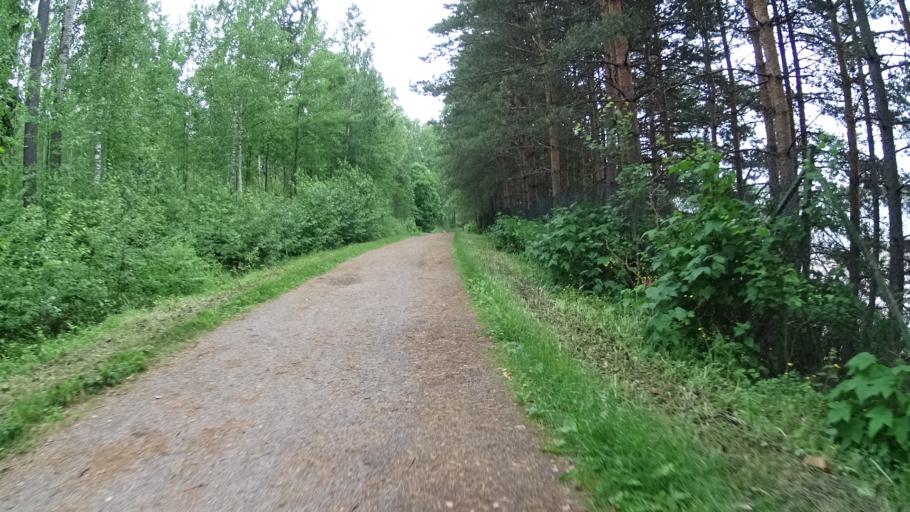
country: FI
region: Uusimaa
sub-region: Helsinki
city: Kilo
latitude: 60.2629
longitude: 24.8379
